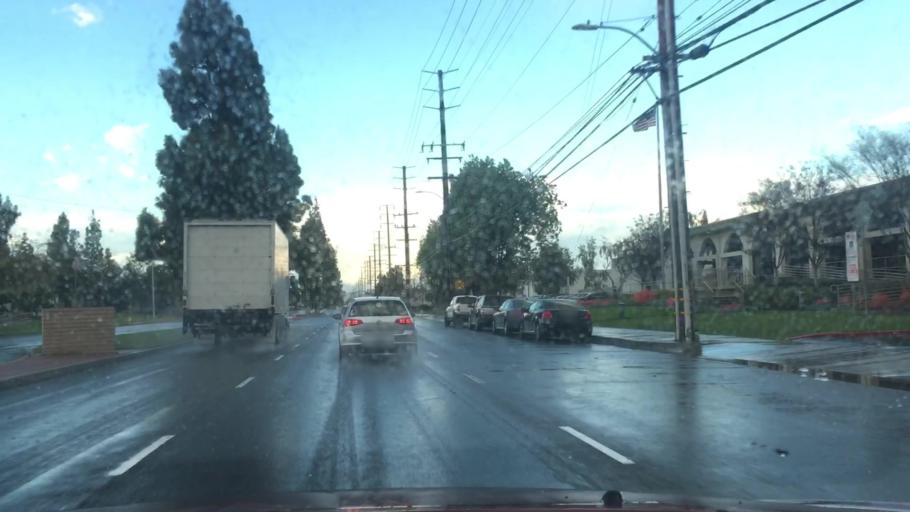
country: US
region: California
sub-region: Orange County
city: La Palma
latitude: 33.8669
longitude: -118.0287
